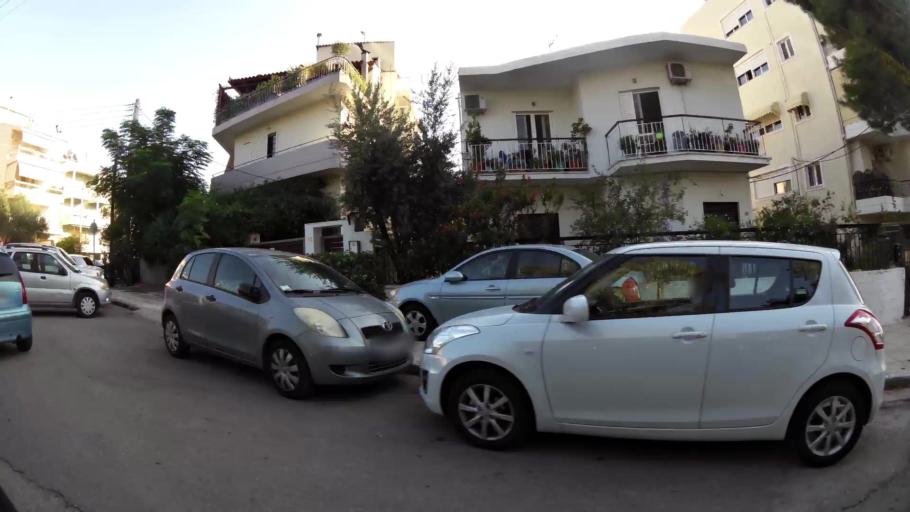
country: GR
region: Attica
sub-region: Nomarchia Athinas
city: Argyroupoli
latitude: 37.8952
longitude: 23.7595
